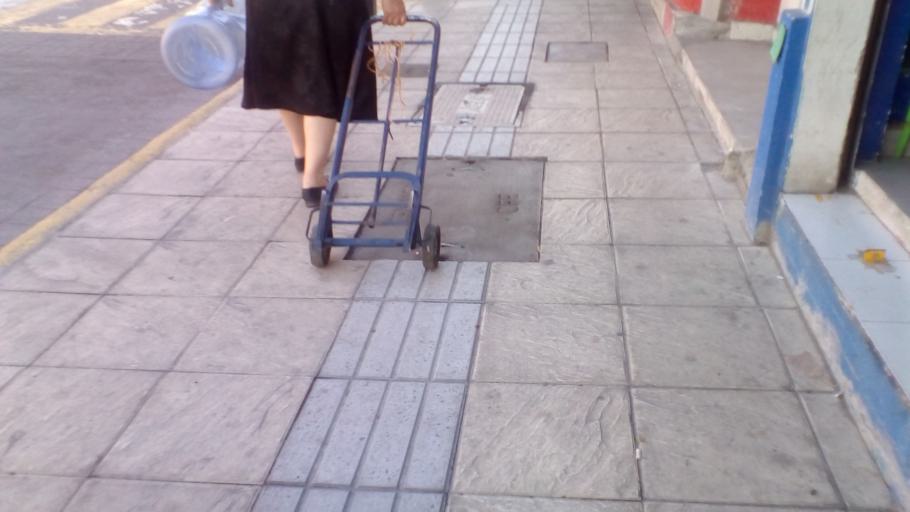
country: MX
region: Guerrero
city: Chilpancingo de los Bravos
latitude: 17.5499
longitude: -99.5006
